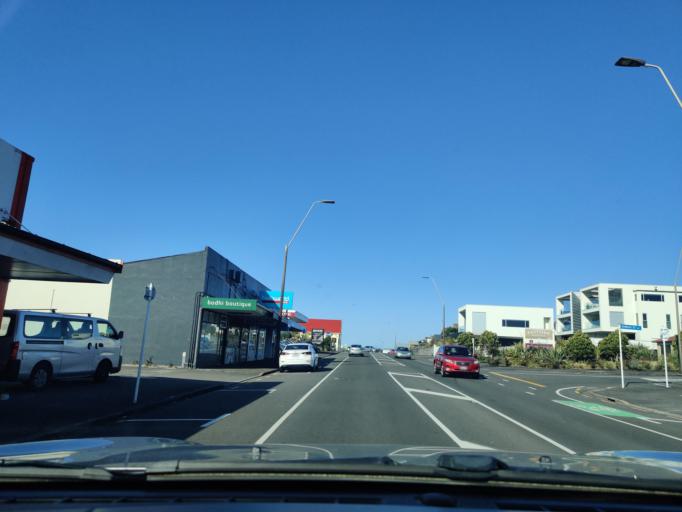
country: NZ
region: Taranaki
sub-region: New Plymouth District
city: New Plymouth
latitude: -39.0509
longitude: 174.0969
